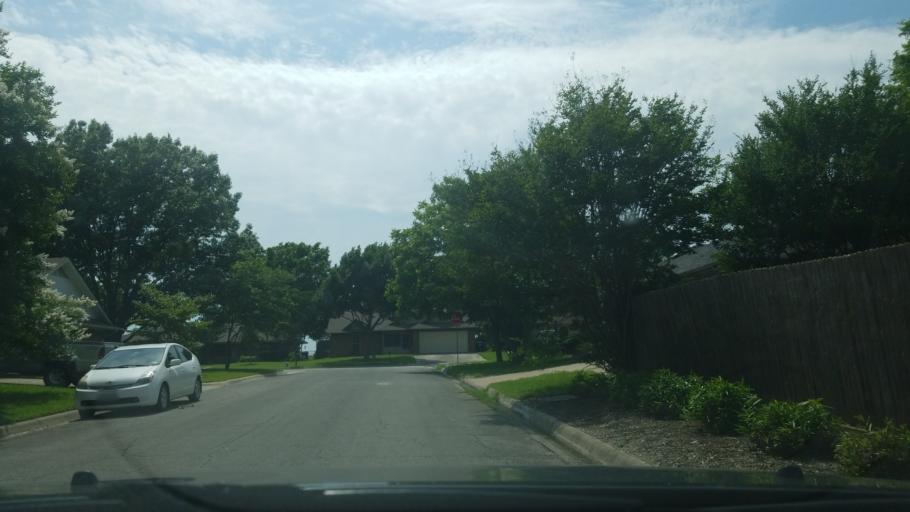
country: US
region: Texas
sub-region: Denton County
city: Denton
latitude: 33.2363
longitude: -97.1528
